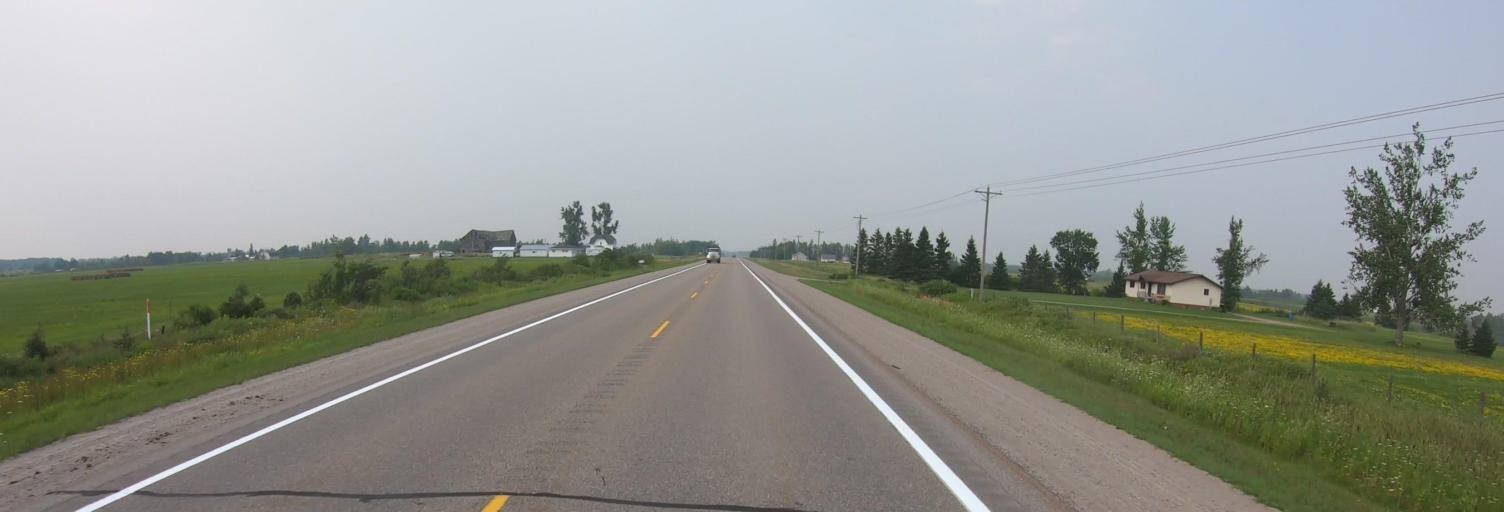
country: US
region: Michigan
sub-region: Chippewa County
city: Sault Ste. Marie
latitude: 46.3409
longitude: -84.3640
